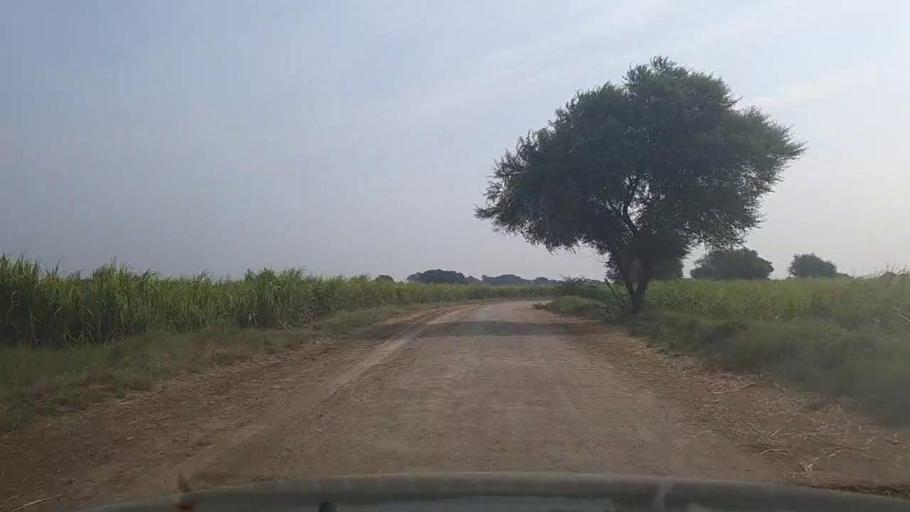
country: PK
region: Sindh
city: Bulri
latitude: 25.0248
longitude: 68.2951
